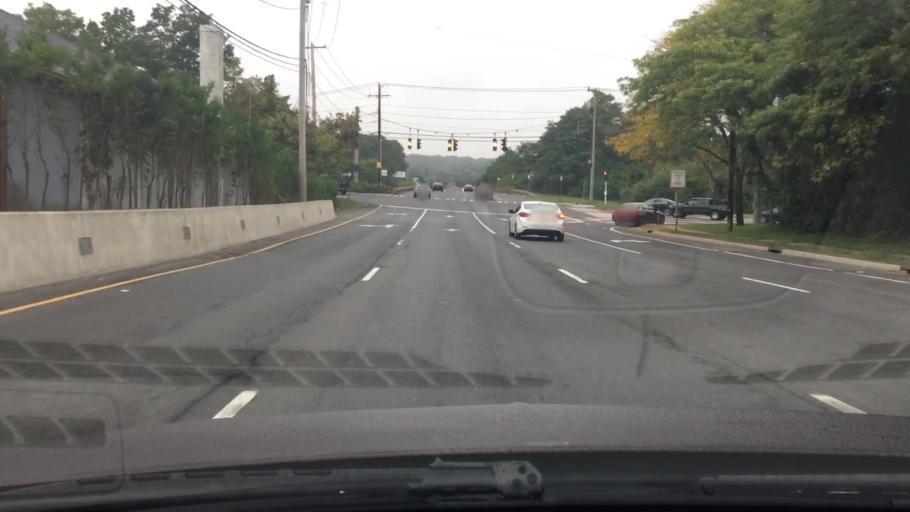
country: US
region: New York
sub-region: Suffolk County
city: Melville
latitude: 40.7820
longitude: -73.4231
